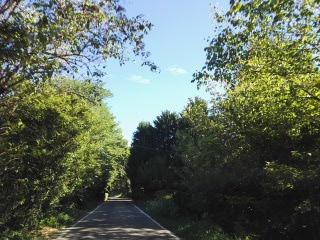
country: IT
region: Lombardy
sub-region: Citta metropolitana di Milano
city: Chiaravalle
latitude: 45.4238
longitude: 9.2172
